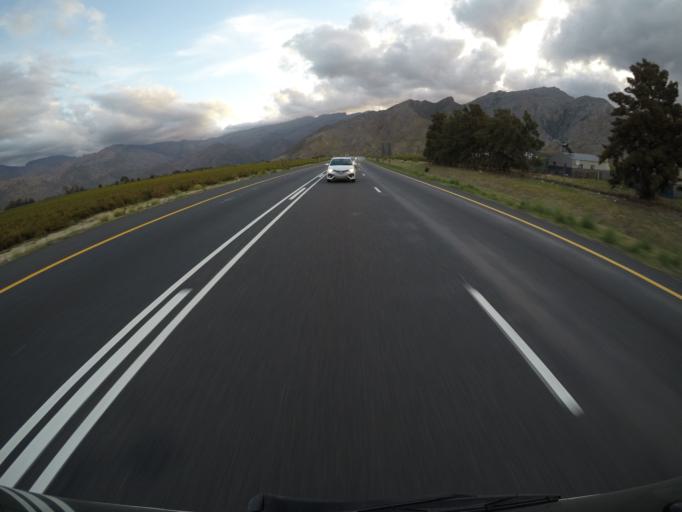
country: ZA
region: Western Cape
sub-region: Cape Winelands District Municipality
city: Worcester
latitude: -33.6825
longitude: 19.2795
